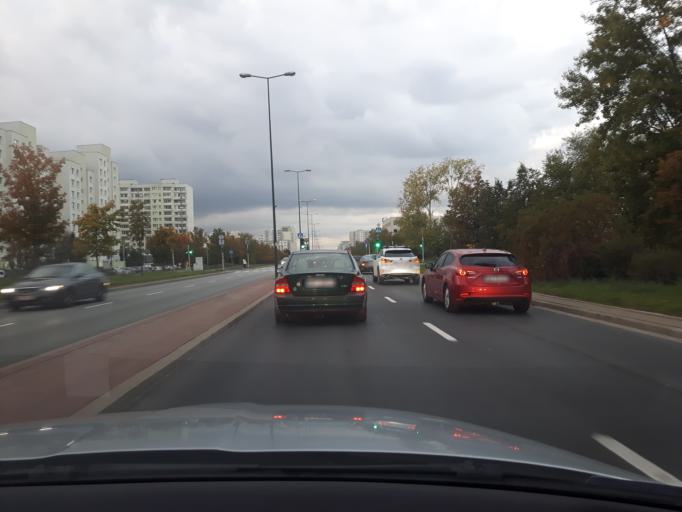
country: PL
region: Masovian Voivodeship
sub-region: Warszawa
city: Ursynow
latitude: 52.1515
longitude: 21.0426
